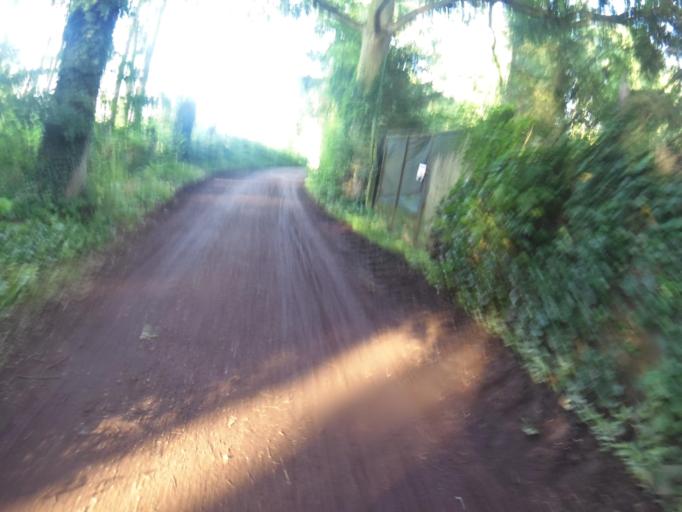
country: BE
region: Flanders
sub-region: Provincie Antwerpen
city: Herselt
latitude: 51.0038
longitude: 4.9135
